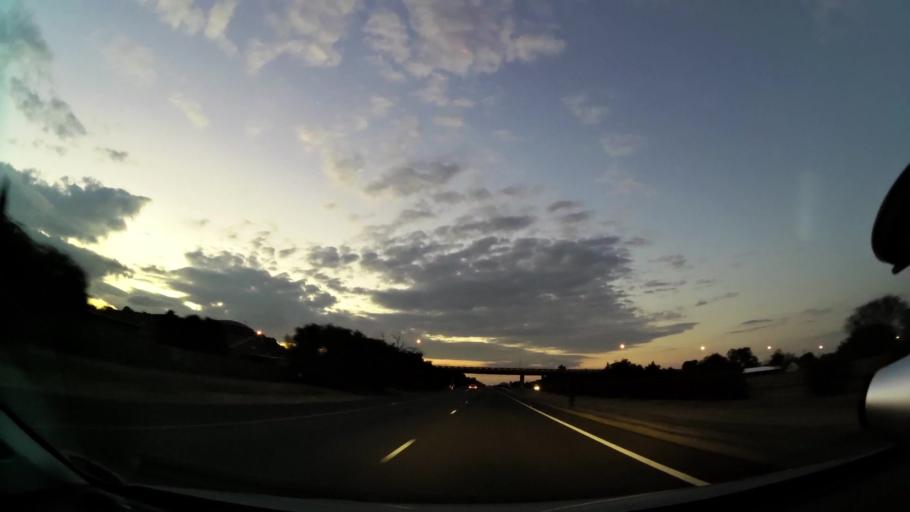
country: ZA
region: Orange Free State
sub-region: Mangaung Metropolitan Municipality
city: Bloemfontein
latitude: -29.1458
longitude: 26.1713
